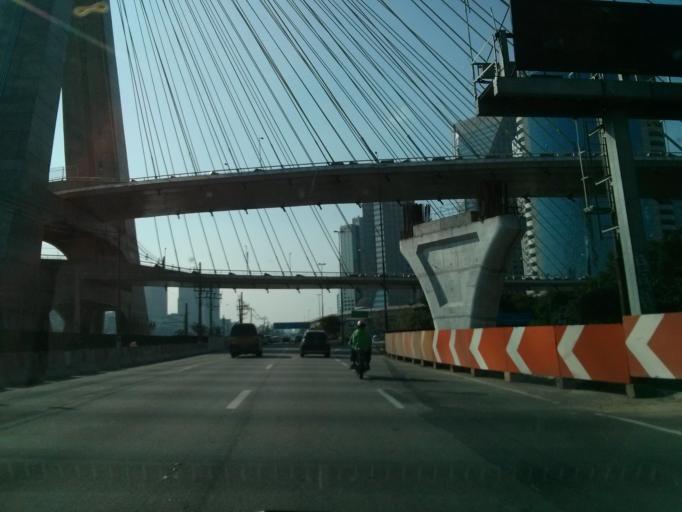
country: BR
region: Sao Paulo
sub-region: Sao Paulo
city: Sao Paulo
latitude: -23.6138
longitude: -46.6988
